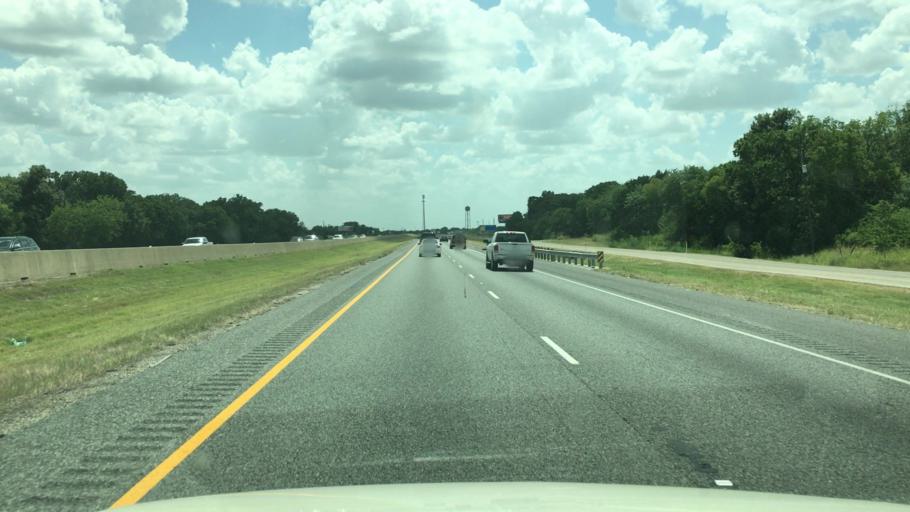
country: US
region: Texas
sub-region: Hunt County
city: Caddo Mills
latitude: 33.0291
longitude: -96.1928
